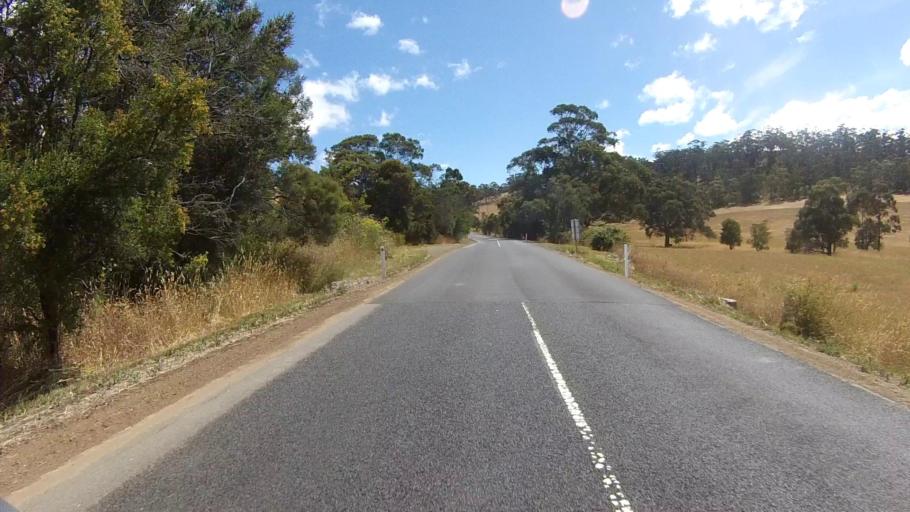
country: AU
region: Tasmania
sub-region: Sorell
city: Sorell
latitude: -42.7421
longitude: 147.4838
